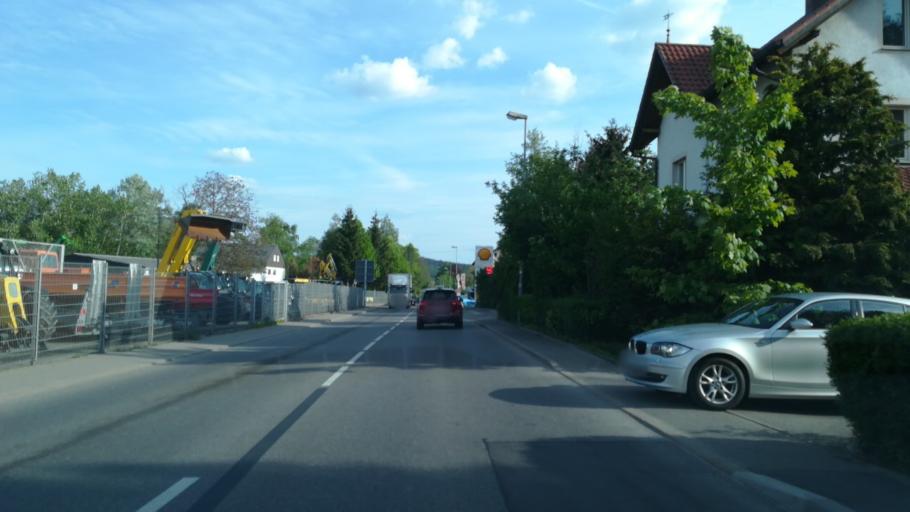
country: DE
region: Baden-Wuerttemberg
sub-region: Freiburg Region
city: Stockach
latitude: 47.8596
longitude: 9.0044
